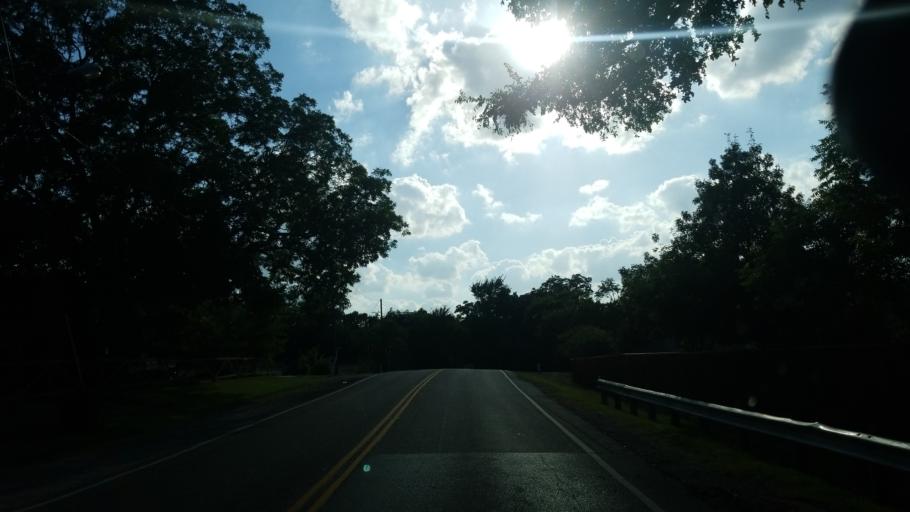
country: US
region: Texas
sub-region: Dallas County
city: Balch Springs
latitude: 32.7781
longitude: -96.7043
